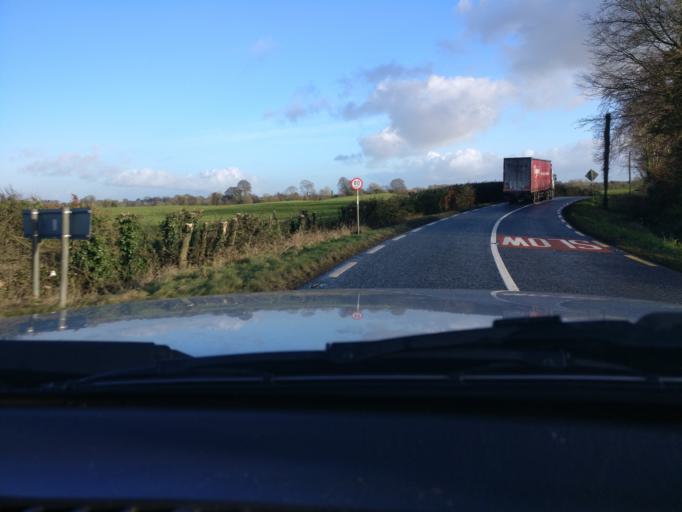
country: IE
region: Leinster
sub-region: An Iarmhi
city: Rathwire
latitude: 53.6263
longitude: -7.0720
